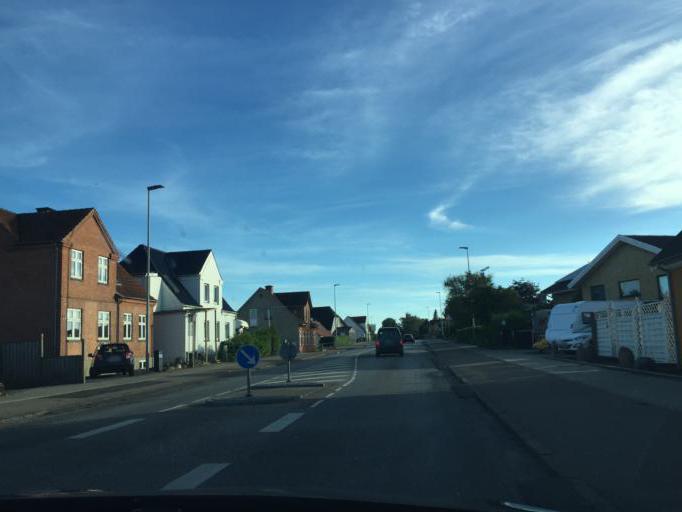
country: DK
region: Zealand
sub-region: Slagelse Kommune
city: Slagelse
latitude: 55.3944
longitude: 11.3346
